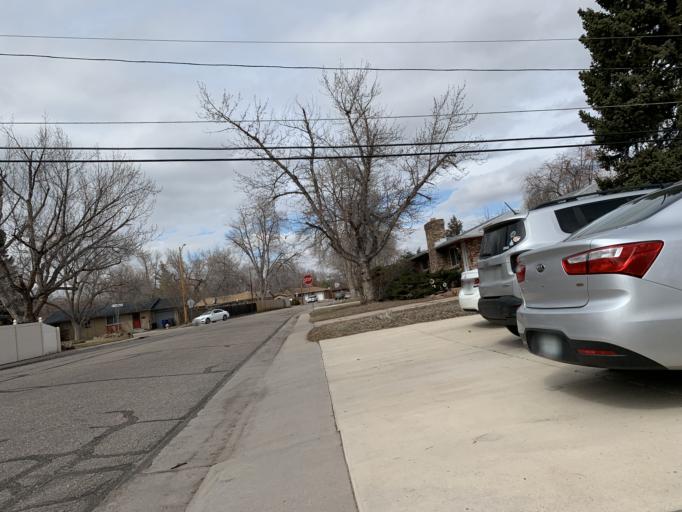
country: US
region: Colorado
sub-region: Arapahoe County
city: Columbine Valley
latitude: 39.6142
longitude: -105.0309
